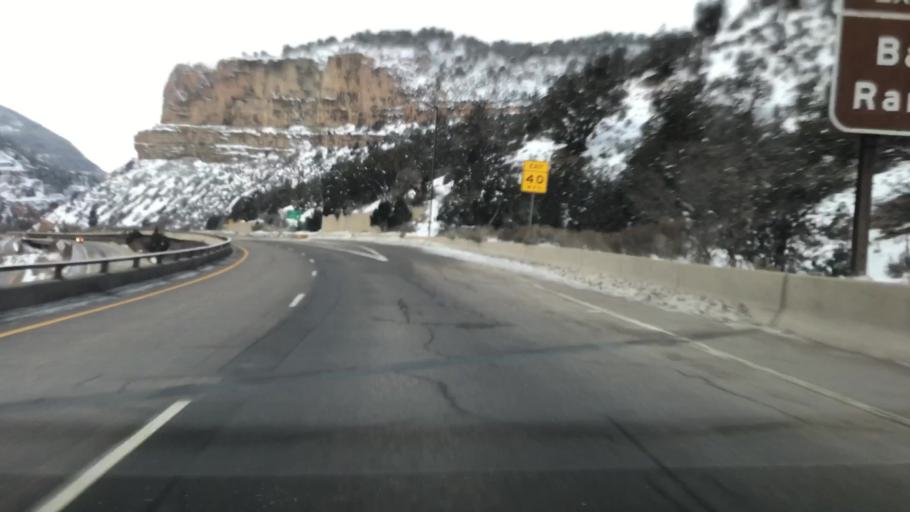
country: US
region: Colorado
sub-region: Eagle County
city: Gypsum
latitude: 39.6156
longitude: -107.1380
